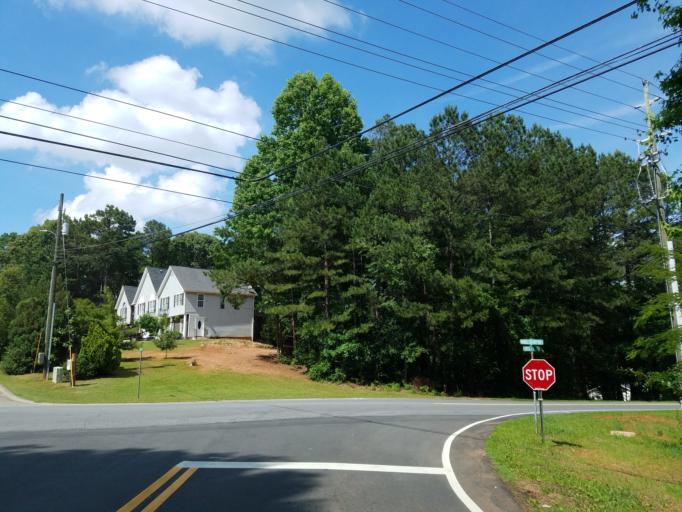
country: US
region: Georgia
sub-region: Cherokee County
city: Holly Springs
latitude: 34.1718
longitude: -84.5108
